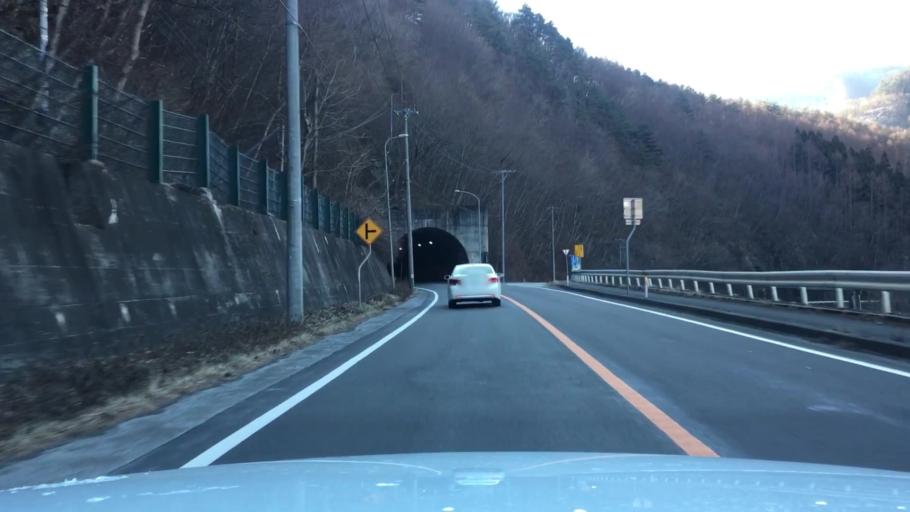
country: JP
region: Iwate
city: Tono
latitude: 39.6387
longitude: 141.6004
